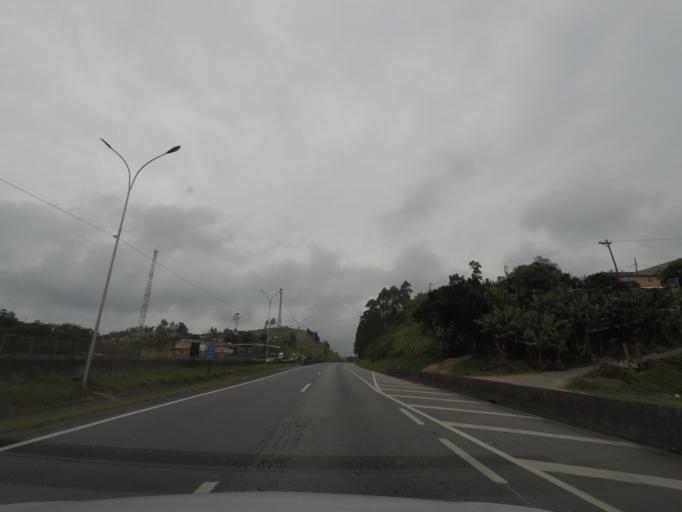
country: BR
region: Sao Paulo
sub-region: Juquitiba
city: Juquitiba
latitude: -23.9823
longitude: -47.1461
